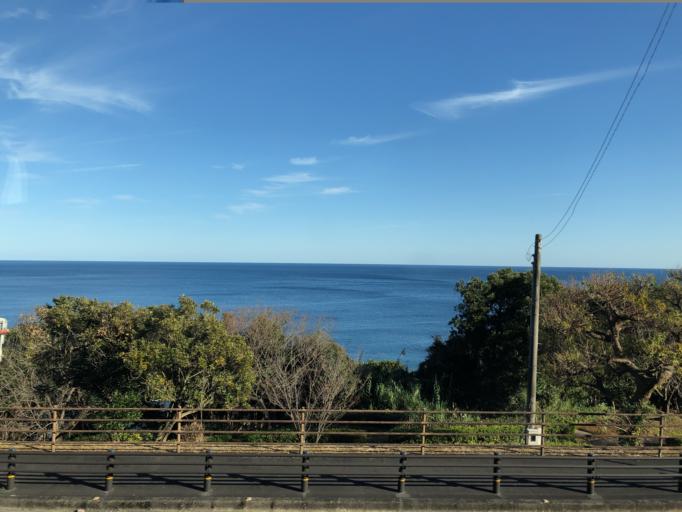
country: JP
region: Kochi
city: Nakamura
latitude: 33.0653
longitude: 133.1068
